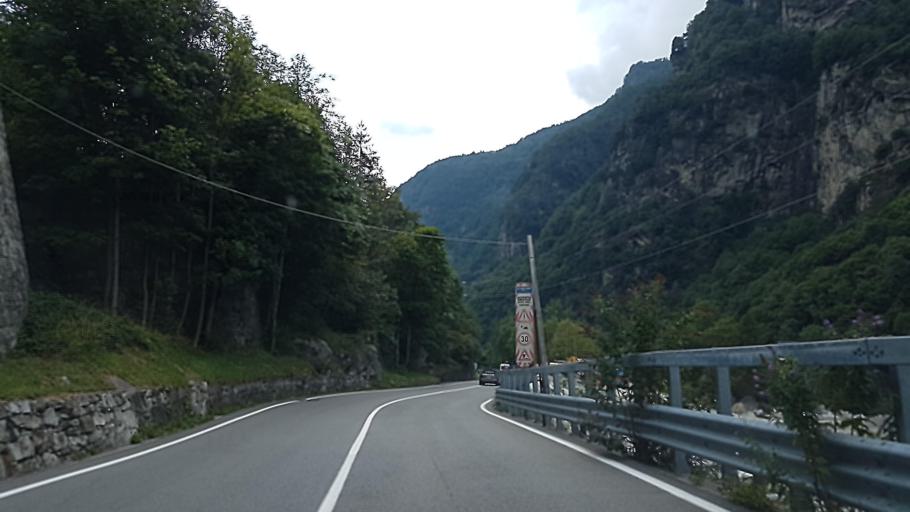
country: IT
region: Lombardy
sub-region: Provincia di Sondrio
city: San Giacomo Filippo
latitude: 46.3615
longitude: 9.3640
